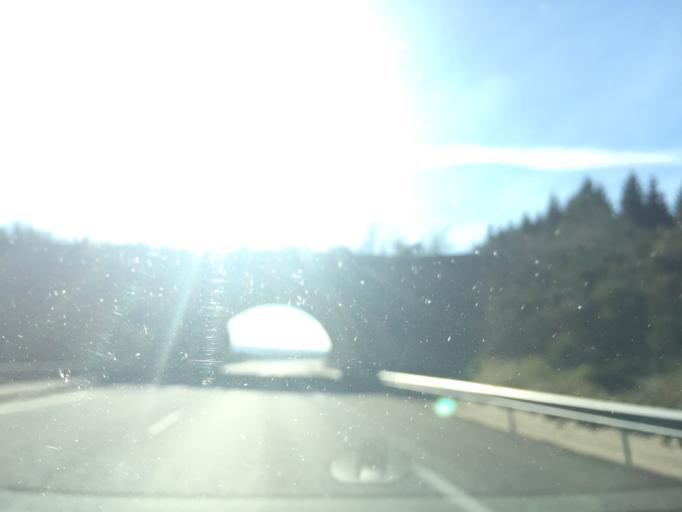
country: FR
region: Auvergne
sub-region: Departement du Puy-de-Dome
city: Gelles
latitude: 45.7066
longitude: 2.6963
